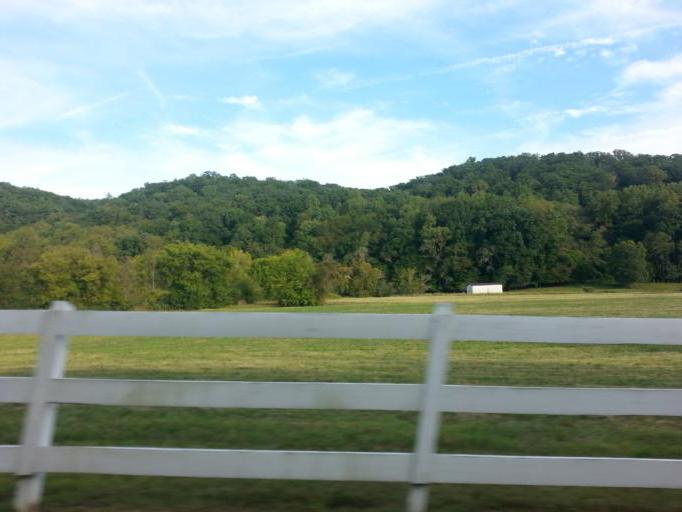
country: US
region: Tennessee
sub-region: Blount County
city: Wildwood
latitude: 35.8352
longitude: -83.8726
